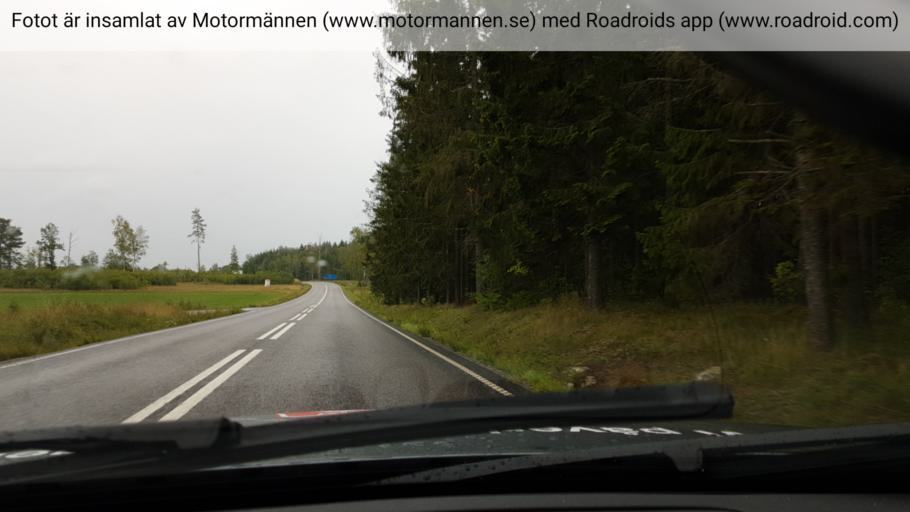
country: SE
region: Soedermanland
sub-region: Eskilstuna Kommun
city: Skogstorp
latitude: 59.3236
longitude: 16.5304
